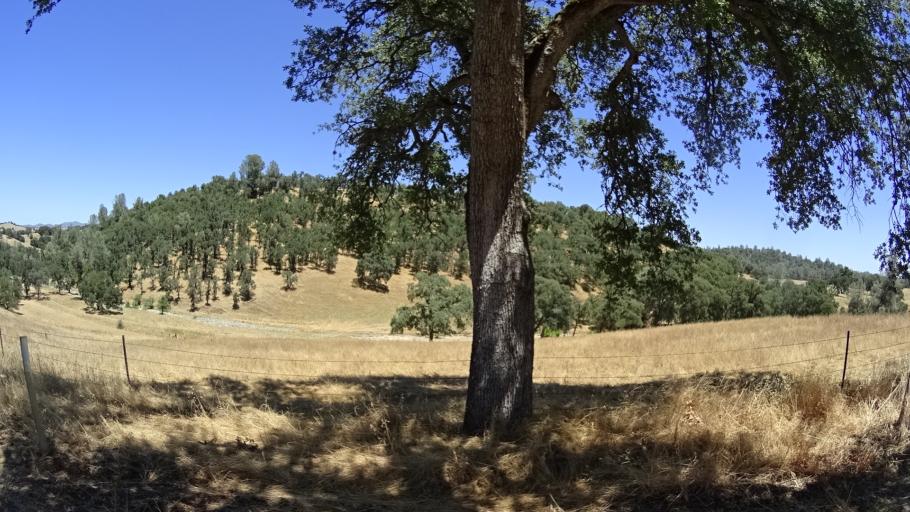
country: US
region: California
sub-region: Calaveras County
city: San Andreas
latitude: 38.1097
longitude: -120.6564
